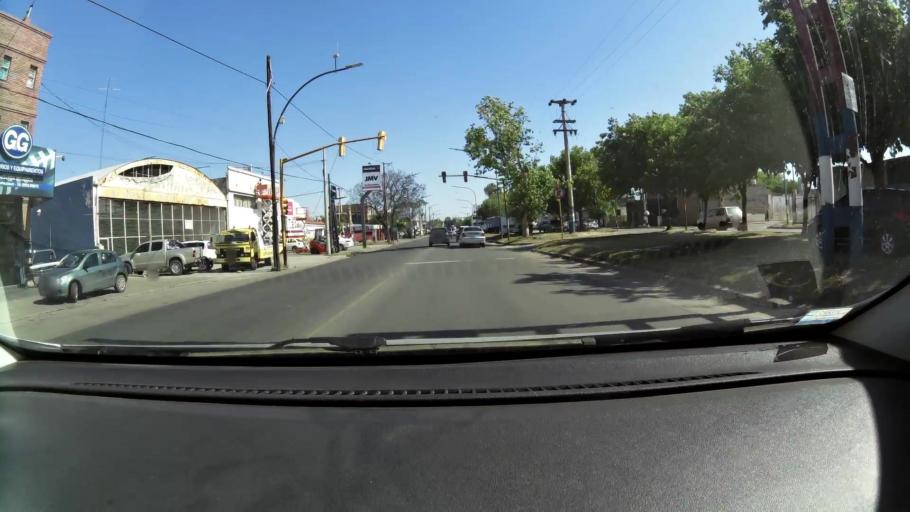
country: AR
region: Cordoba
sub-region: Departamento de Capital
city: Cordoba
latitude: -31.3684
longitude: -64.1762
